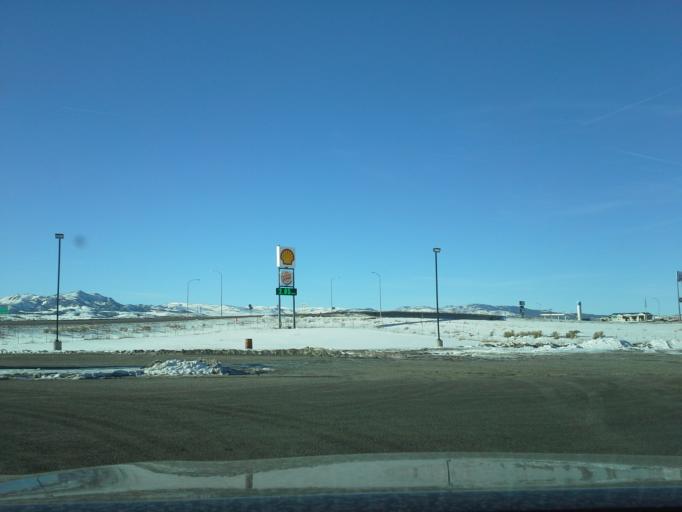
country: US
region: Utah
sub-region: Beaver County
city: Beaver
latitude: 38.2509
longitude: -112.6477
